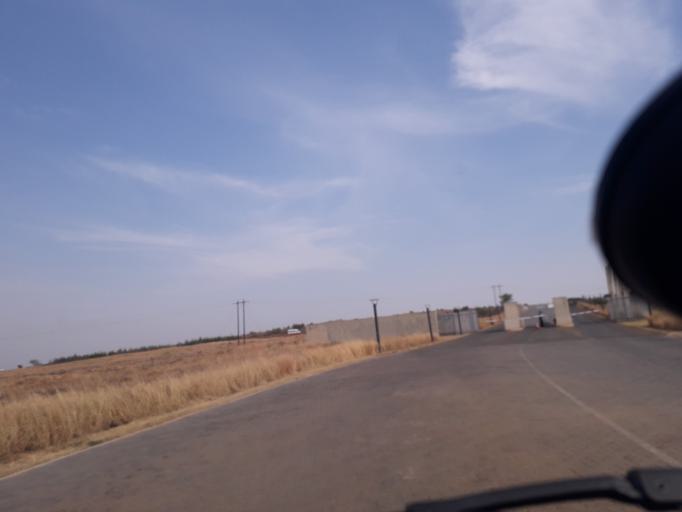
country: ZA
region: Gauteng
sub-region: West Rand District Municipality
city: Krugersdorp
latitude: -25.9769
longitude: 27.6641
